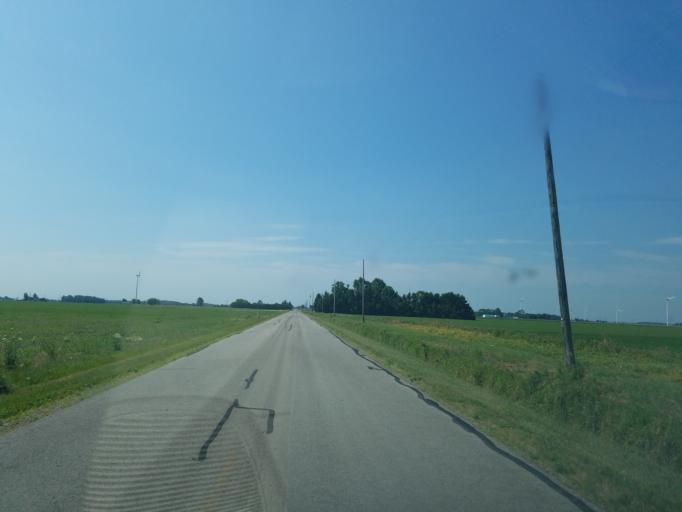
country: US
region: Ohio
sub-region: Van Wert County
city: Convoy
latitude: 40.9576
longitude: -84.6299
